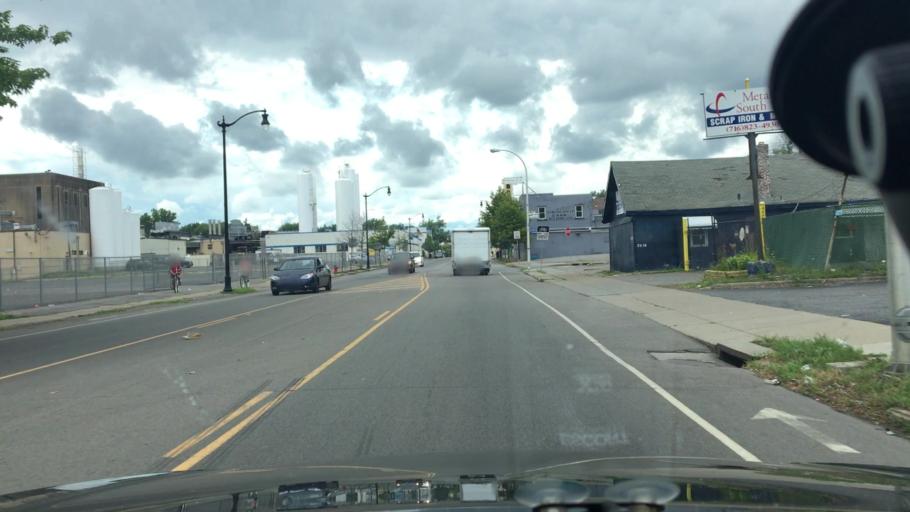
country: US
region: New York
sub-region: Erie County
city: Lackawanna
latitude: 42.8314
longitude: -78.8239
